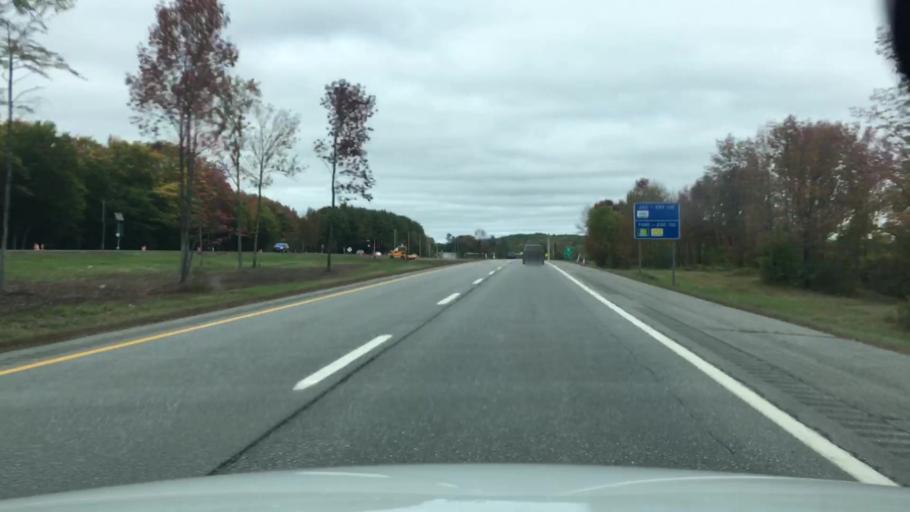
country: US
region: Maine
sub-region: Somerset County
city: Fairfield
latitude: 44.5874
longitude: -69.6211
